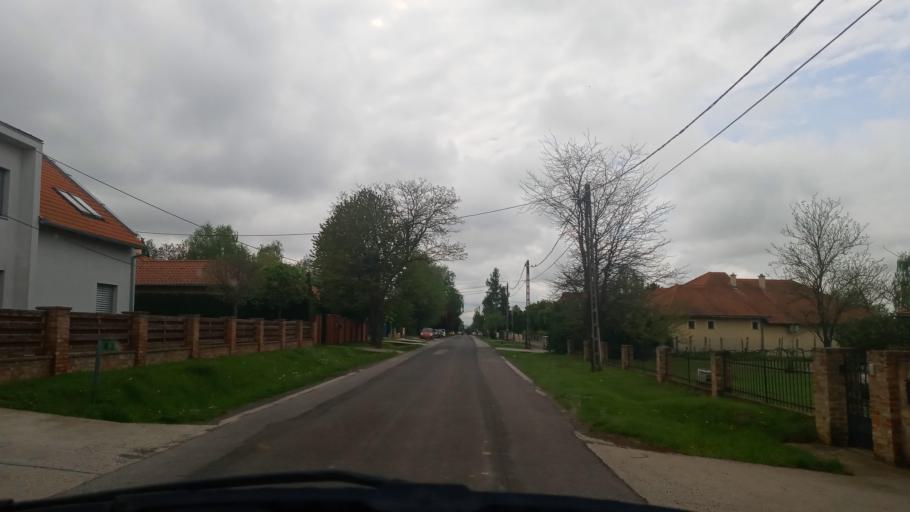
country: HU
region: Baranya
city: Kozarmisleny
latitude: 46.0054
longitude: 18.3745
